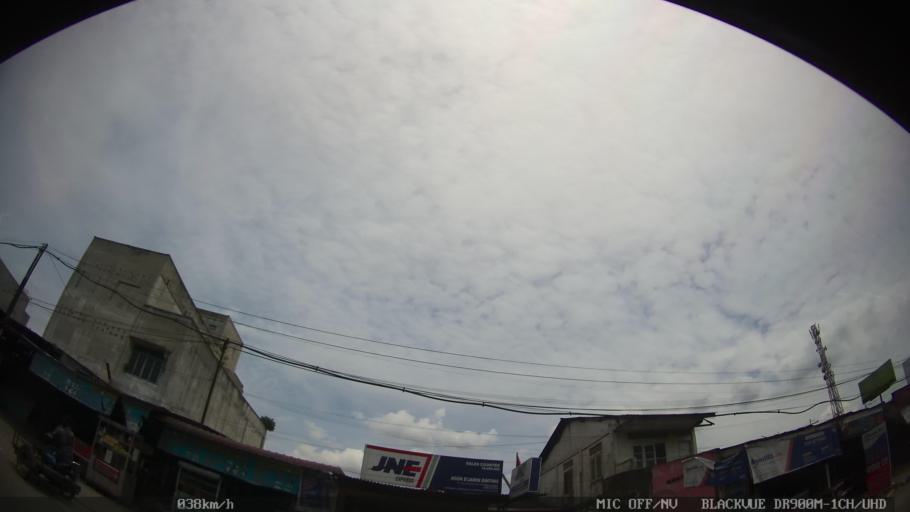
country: ID
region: North Sumatra
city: Deli Tua
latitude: 3.5278
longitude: 98.6353
